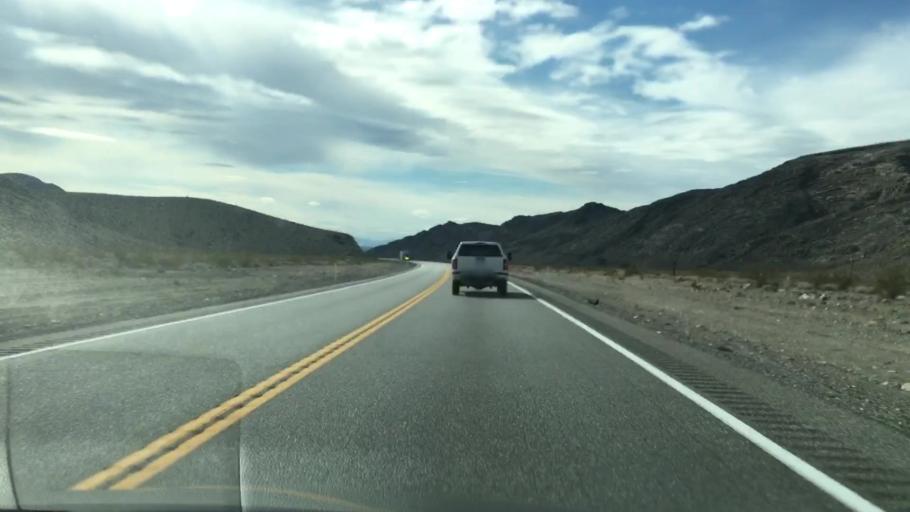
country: US
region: Nevada
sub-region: Nye County
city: Pahrump
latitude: 36.5845
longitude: -116.0614
